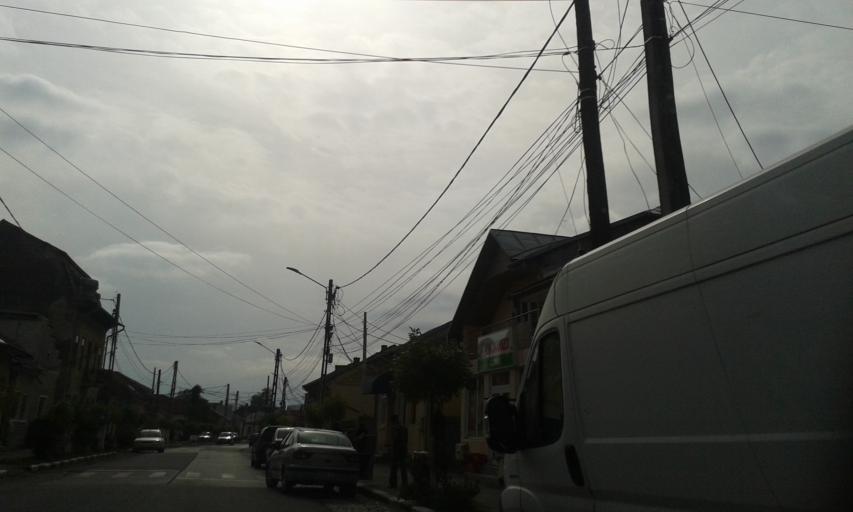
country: RO
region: Gorj
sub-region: Comuna Targu Carbunesti
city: Targu Carbunesti
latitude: 44.9540
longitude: 23.5140
